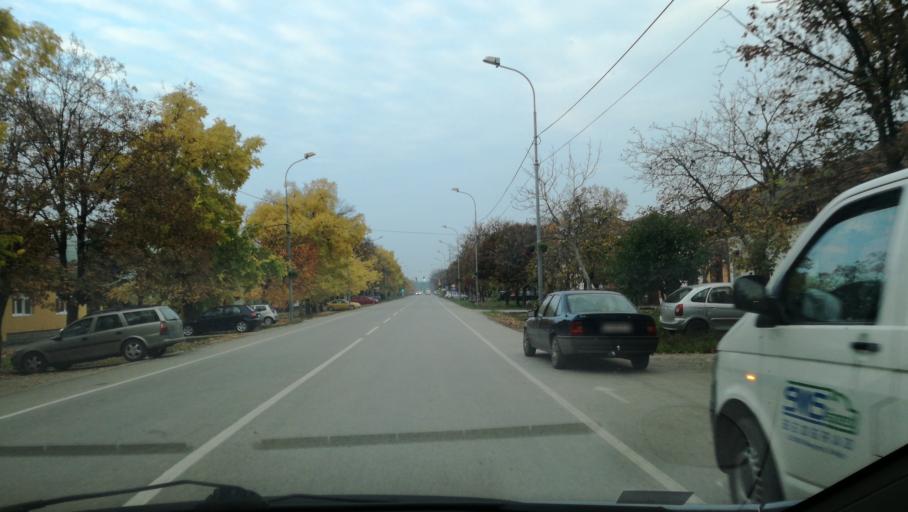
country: RS
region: Autonomna Pokrajina Vojvodina
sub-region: Severnobanatski Okrug
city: Kikinda
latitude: 45.8246
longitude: 20.4566
